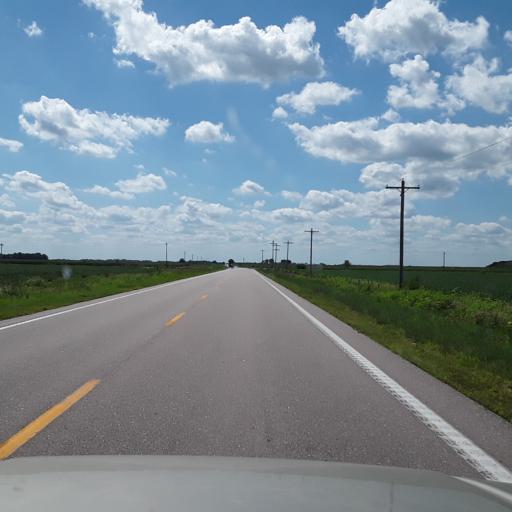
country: US
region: Nebraska
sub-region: Merrick County
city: Central City
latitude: 41.1914
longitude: -98.0556
